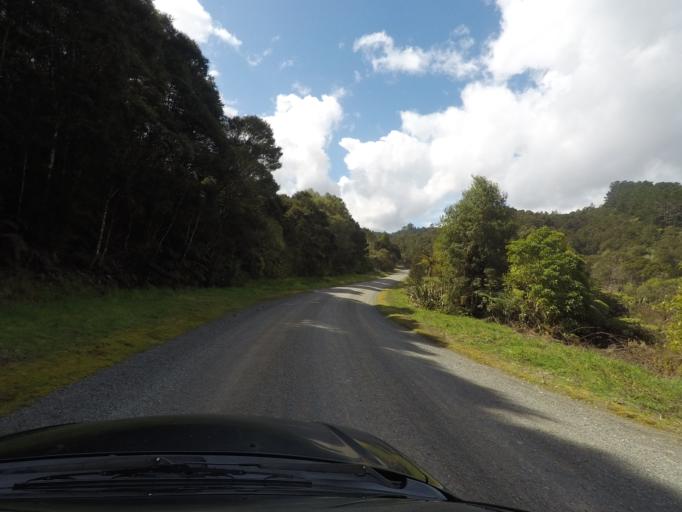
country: NZ
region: Auckland
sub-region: Auckland
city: Red Hill
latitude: -37.0942
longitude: 175.1517
